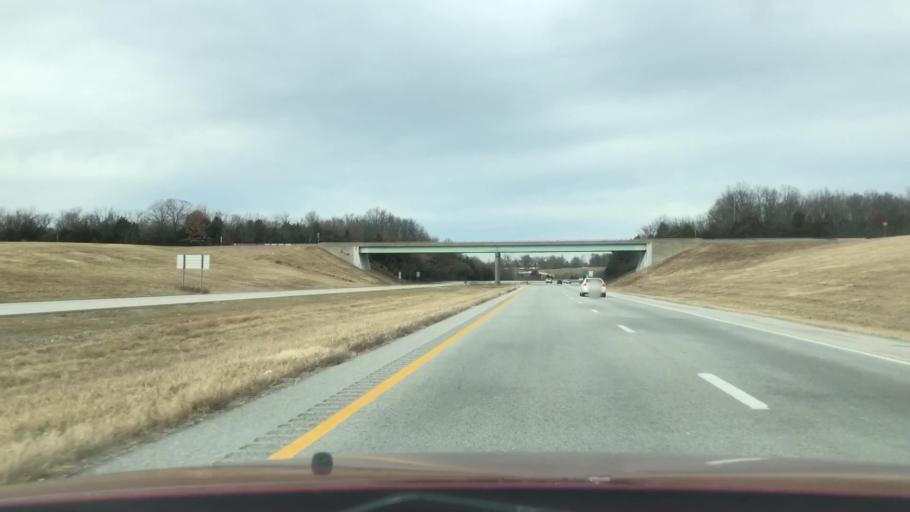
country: US
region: Missouri
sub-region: Greene County
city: Springfield
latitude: 37.2590
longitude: -93.2247
